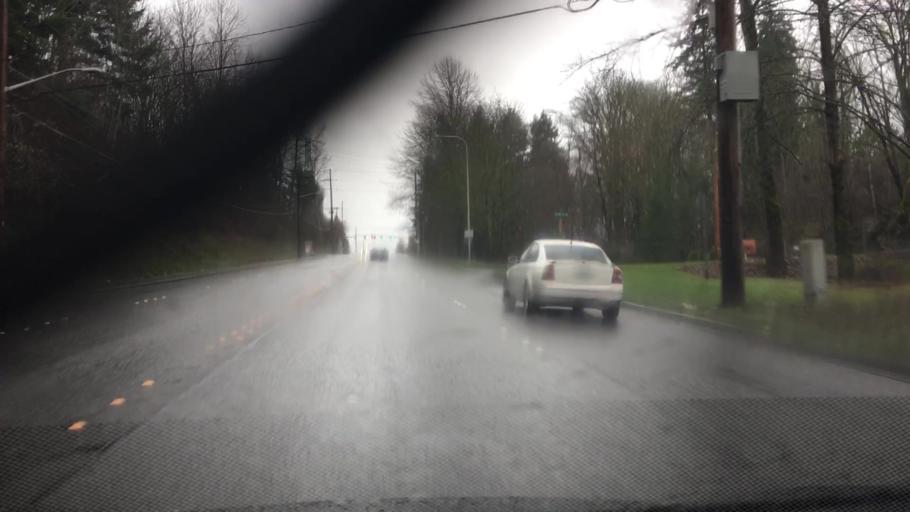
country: US
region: Washington
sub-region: King County
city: Renton
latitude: 47.4852
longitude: -122.1894
